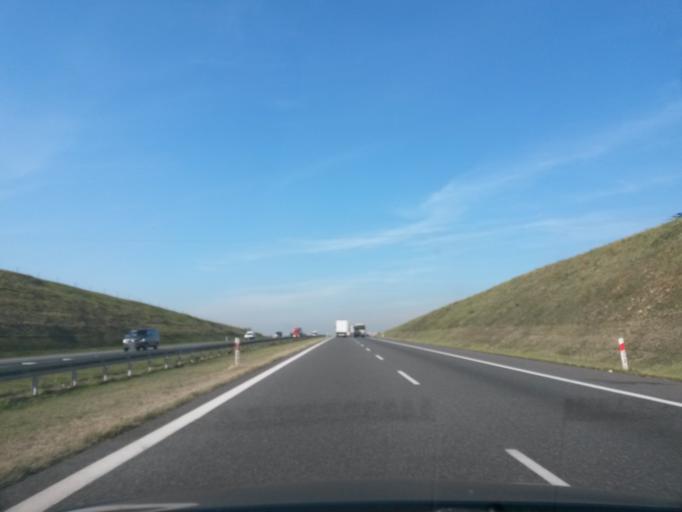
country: PL
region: Silesian Voivodeship
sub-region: Powiat bierunsko-ledzinski
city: Imielin
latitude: 50.1639
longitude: 19.2222
